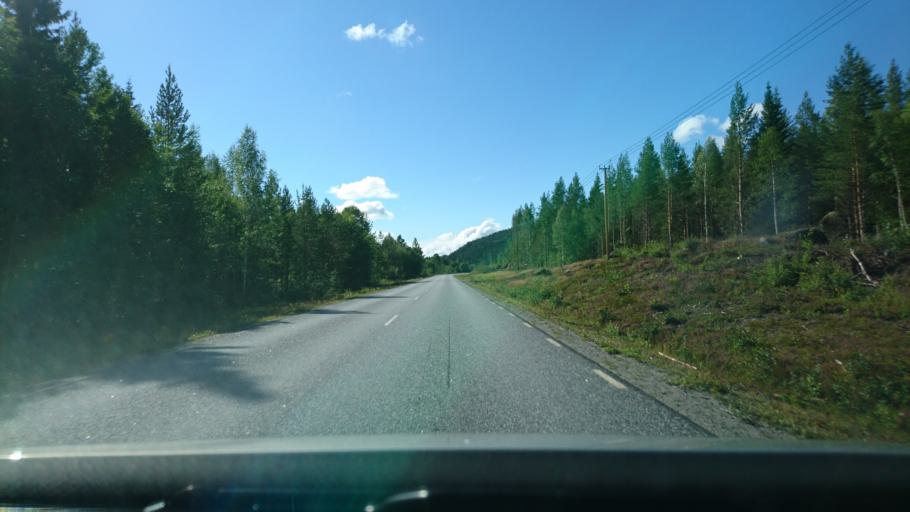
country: SE
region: Vaesterbotten
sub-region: Asele Kommun
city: Asele
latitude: 64.3212
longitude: 17.1081
